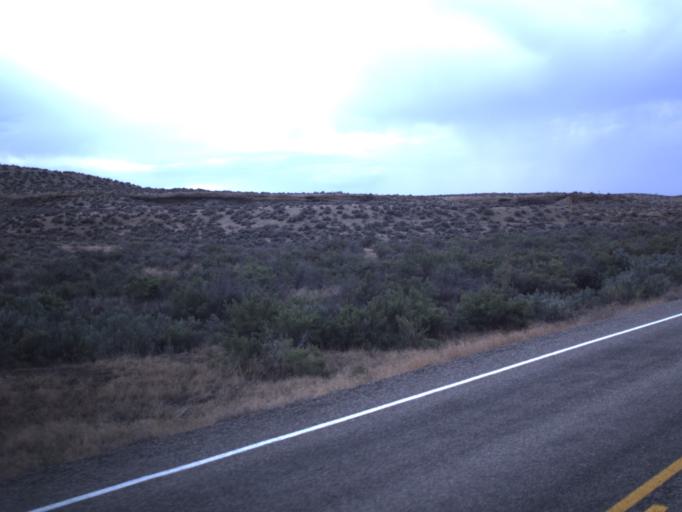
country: US
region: Colorado
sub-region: Rio Blanco County
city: Rangely
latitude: 40.0319
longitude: -109.1807
